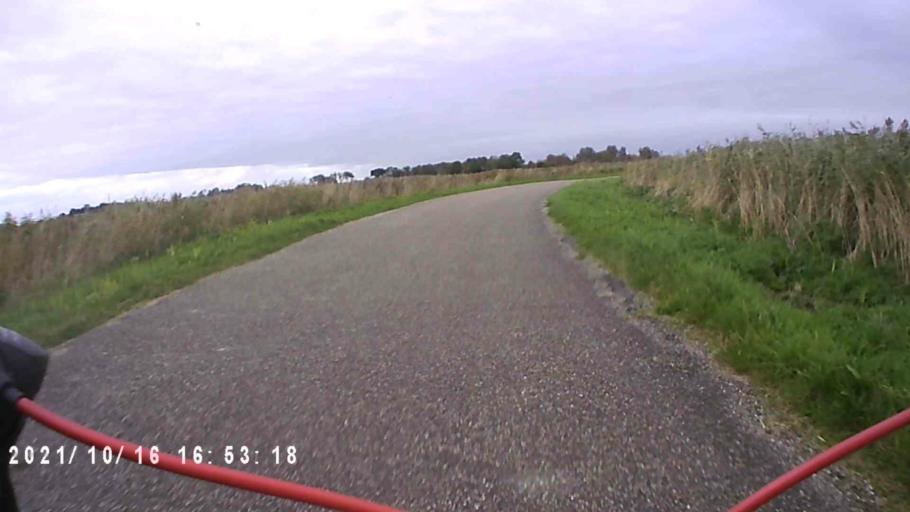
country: NL
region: Friesland
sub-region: Gemeente Dongeradeel
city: Anjum
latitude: 53.3538
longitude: 6.1511
